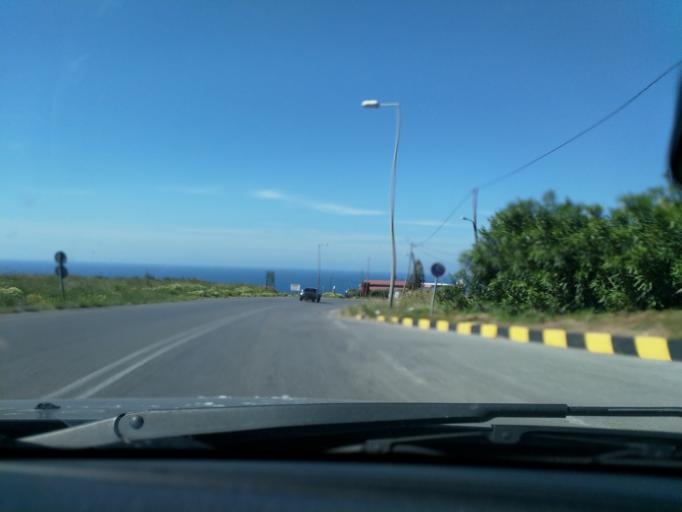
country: GR
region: Crete
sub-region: Nomos Rethymnis
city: Rethymno
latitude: 35.3534
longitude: 24.4611
